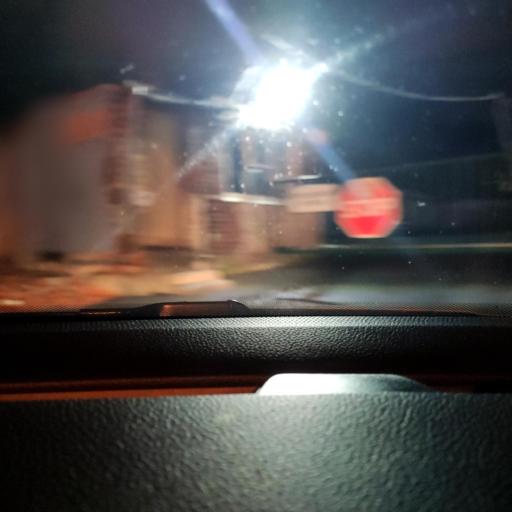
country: RU
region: Moscow
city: Otradnoye
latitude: 55.8553
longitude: 37.5948
